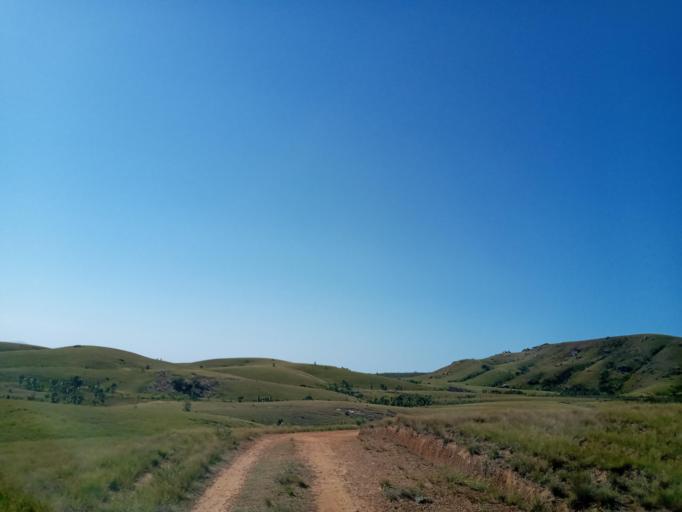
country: MG
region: Anosy
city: Fort Dauphin
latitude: -24.9096
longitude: 47.0753
